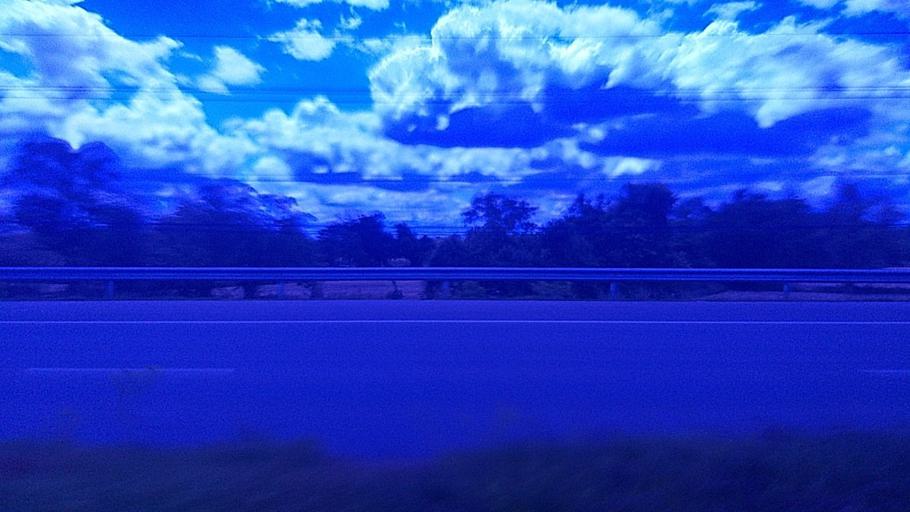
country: TH
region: Nakhon Ratchasima
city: Dan Khun Thot
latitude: 15.2809
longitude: 101.7951
